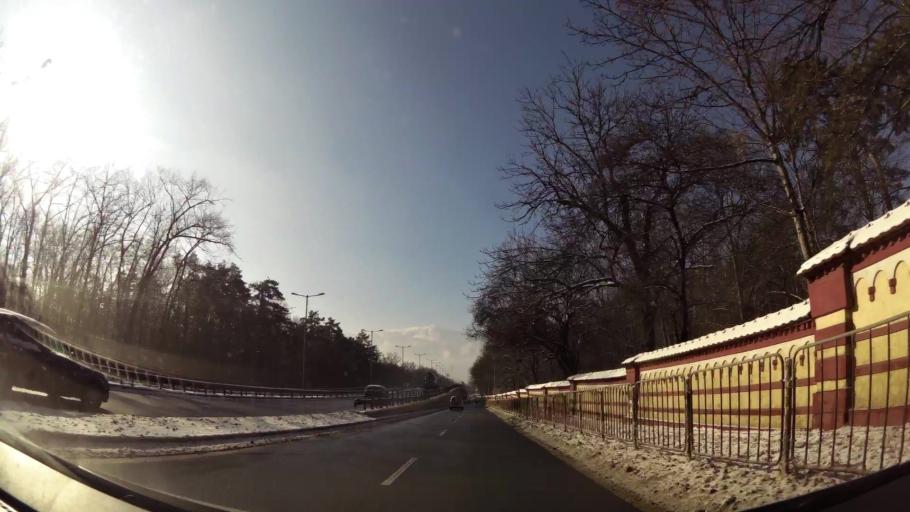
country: BG
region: Sofia-Capital
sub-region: Stolichna Obshtina
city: Sofia
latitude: 42.6742
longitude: 23.3378
